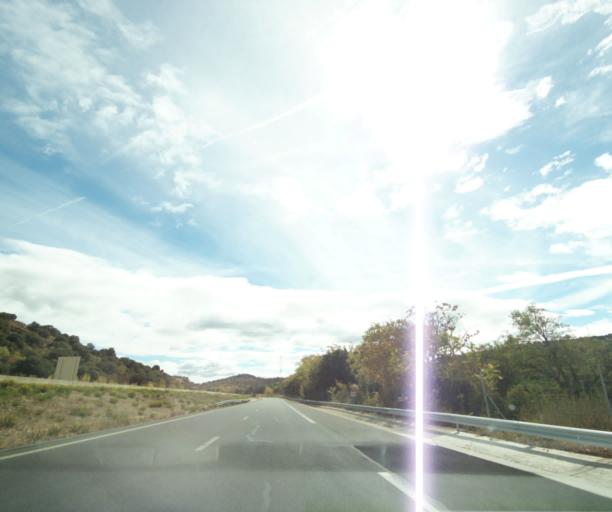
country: FR
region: Languedoc-Roussillon
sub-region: Departement de l'Herault
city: Lodeve
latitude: 43.7028
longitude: 3.3295
